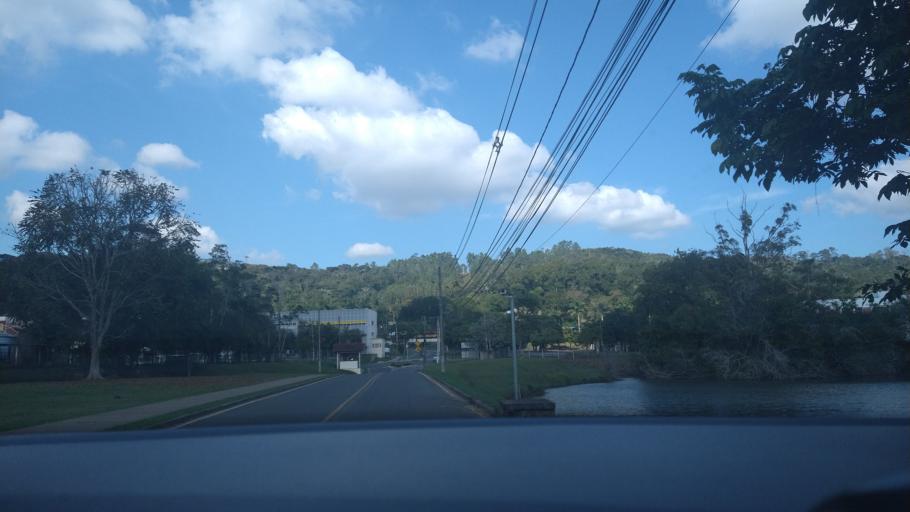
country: BR
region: Minas Gerais
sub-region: Vicosa
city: Vicosa
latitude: -20.7707
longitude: -42.8745
